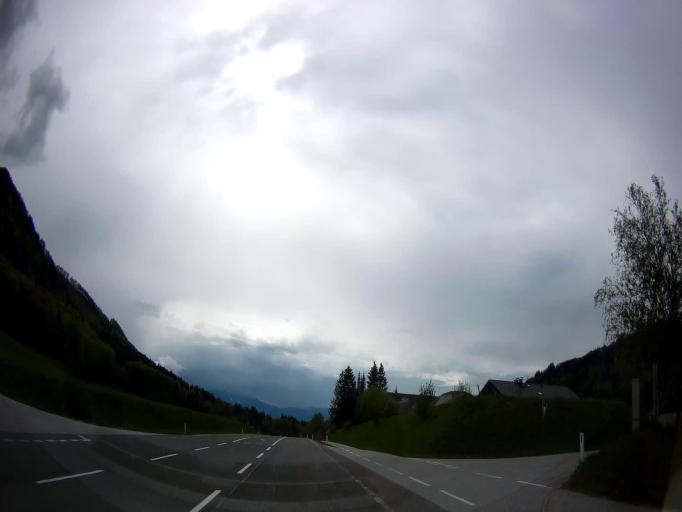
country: AT
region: Salzburg
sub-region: Politischer Bezirk Salzburg-Umgebung
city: Koppl
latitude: 47.8224
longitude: 13.1217
